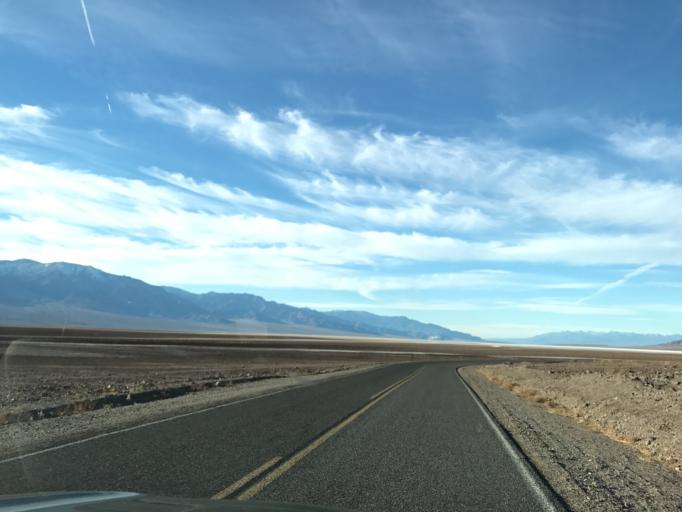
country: US
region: Nevada
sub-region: Nye County
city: Beatty
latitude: 36.2066
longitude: -116.7759
